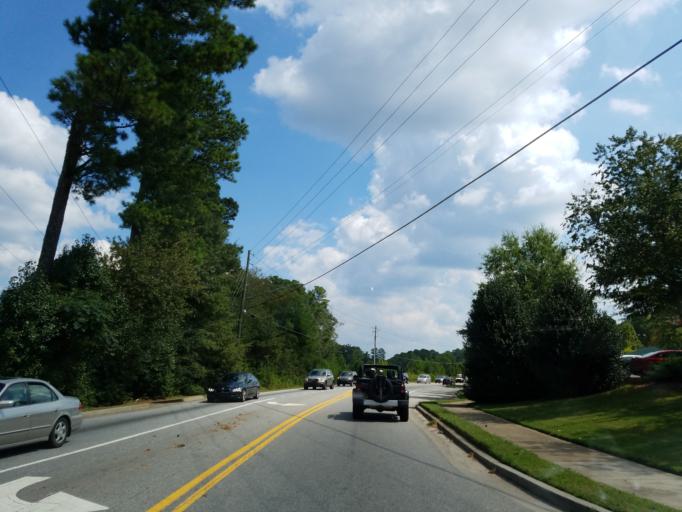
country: US
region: Georgia
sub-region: Fulton County
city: Alpharetta
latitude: 34.0608
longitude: -84.3024
